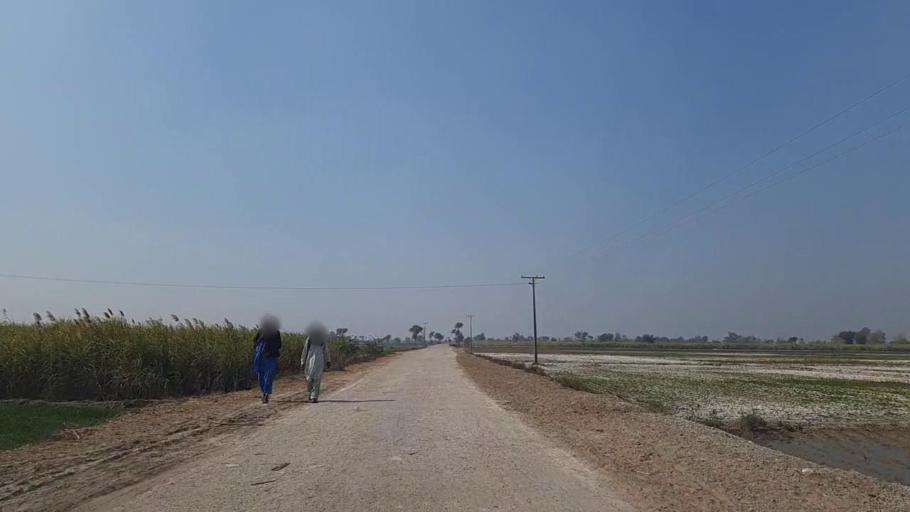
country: PK
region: Sindh
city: Daur
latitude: 26.5032
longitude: 68.3204
